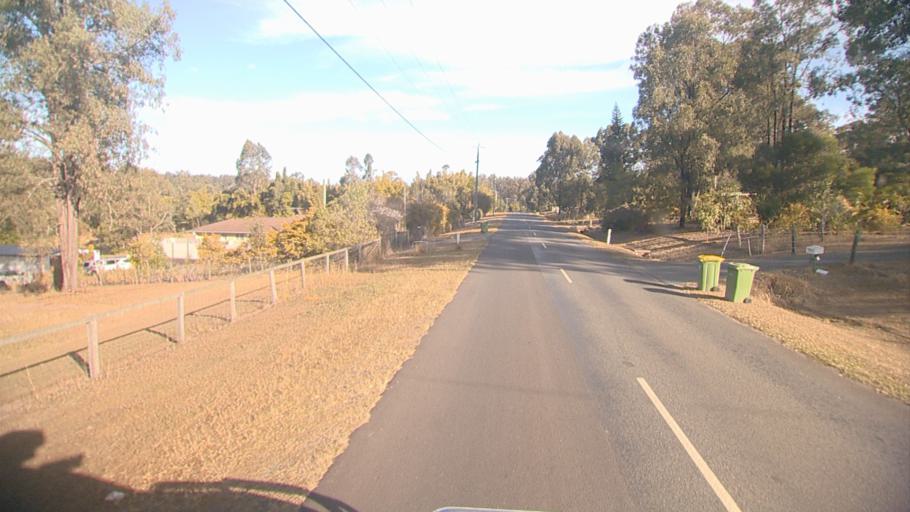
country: AU
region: Queensland
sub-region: Logan
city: Cedar Vale
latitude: -27.8767
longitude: 153.0106
